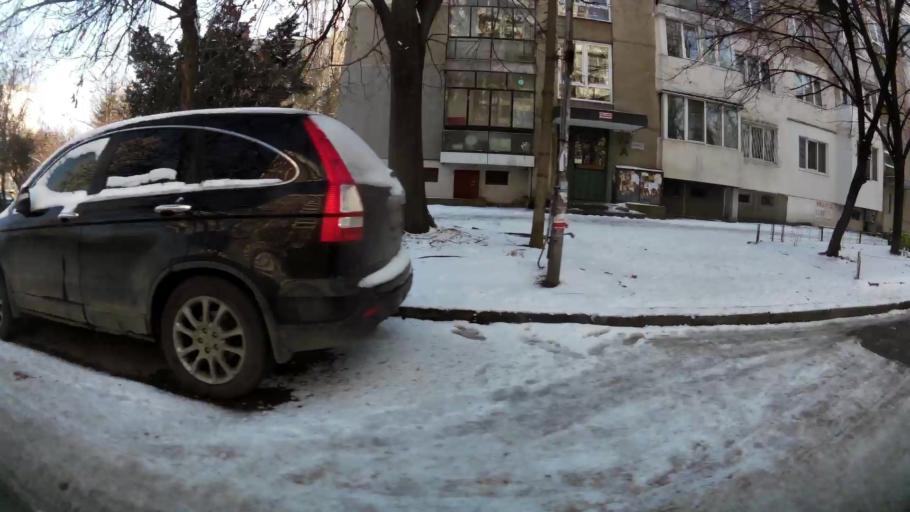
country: BG
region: Sofia-Capital
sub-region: Stolichna Obshtina
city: Sofia
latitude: 42.6637
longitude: 23.3491
